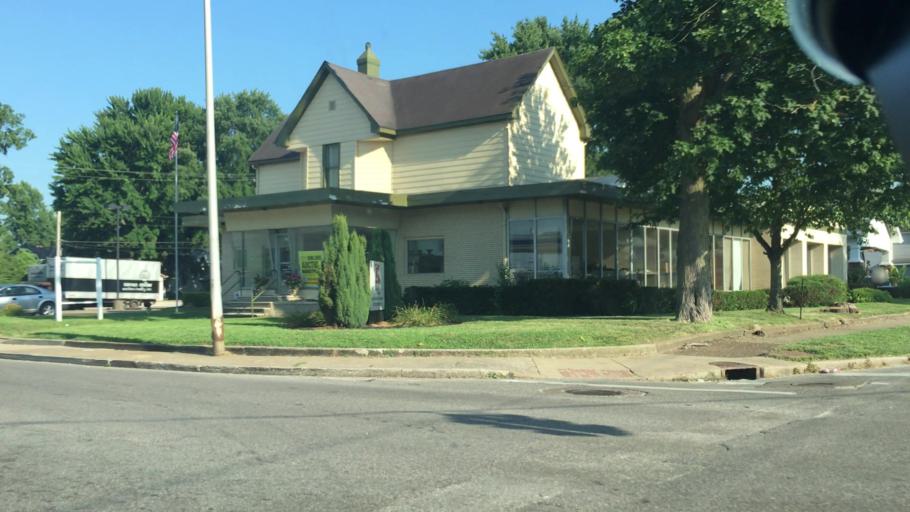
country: US
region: Indiana
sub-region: Vanderburgh County
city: Evansville
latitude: 37.9736
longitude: -87.5476
